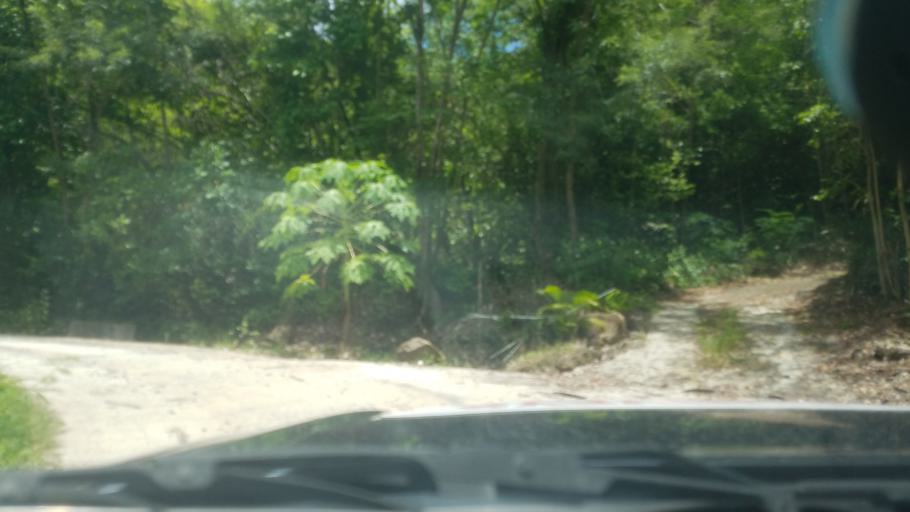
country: LC
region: Praslin
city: Praslin
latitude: 13.8670
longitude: -60.9057
